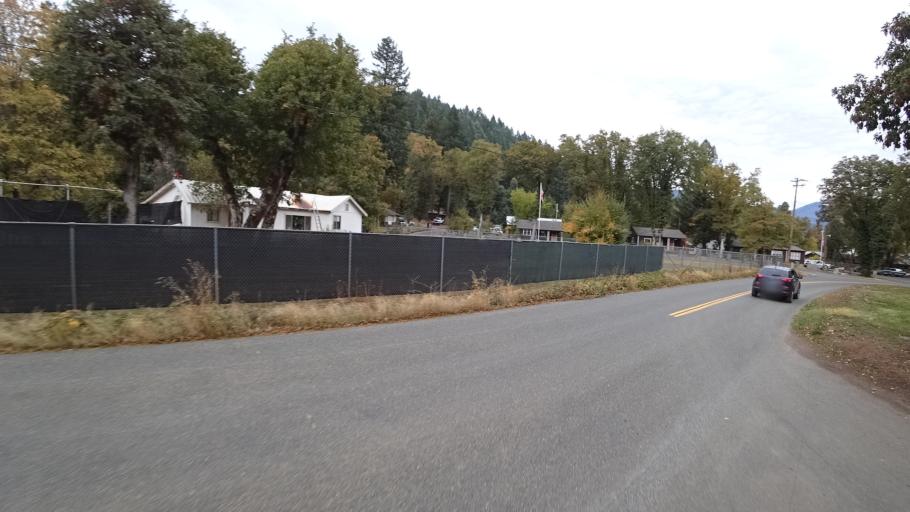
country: US
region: California
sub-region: Siskiyou County
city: Happy Camp
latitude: 41.7920
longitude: -123.3817
